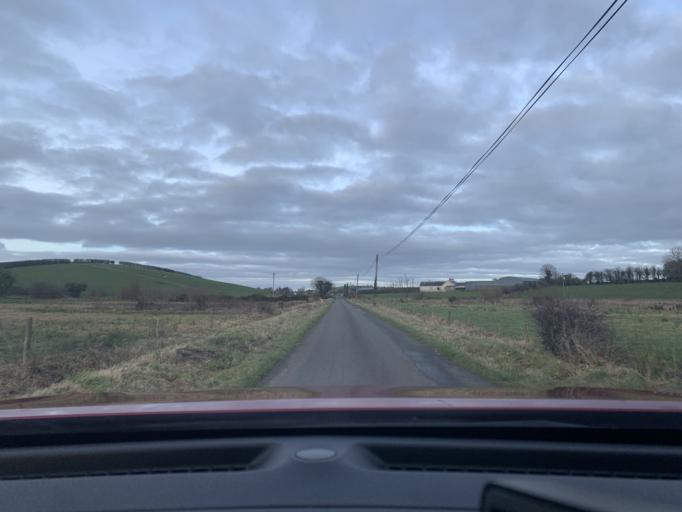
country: IE
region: Connaught
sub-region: Sligo
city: Ballymote
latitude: 54.0507
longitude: -8.5700
